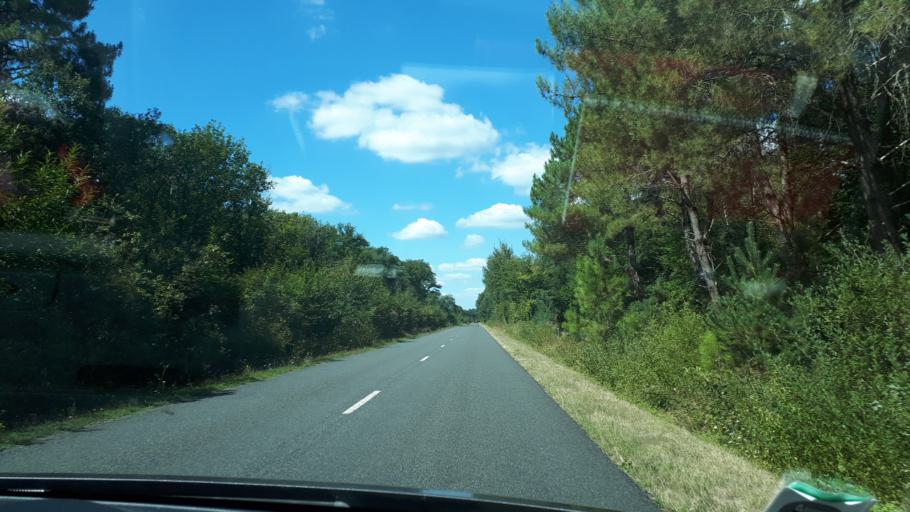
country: FR
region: Centre
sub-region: Departement du Loir-et-Cher
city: Dhuizon
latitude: 47.5345
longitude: 1.6986
